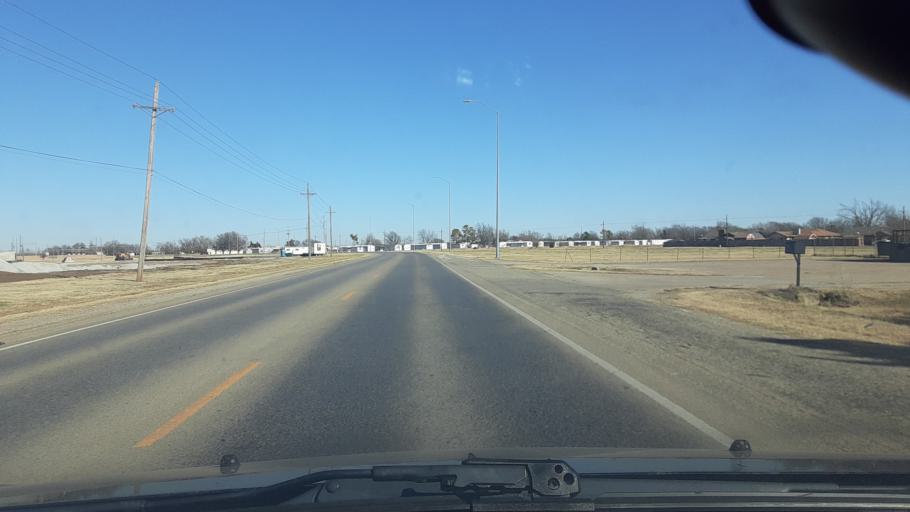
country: US
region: Oklahoma
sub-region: Kay County
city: Ponca City
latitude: 36.7327
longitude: -97.0918
